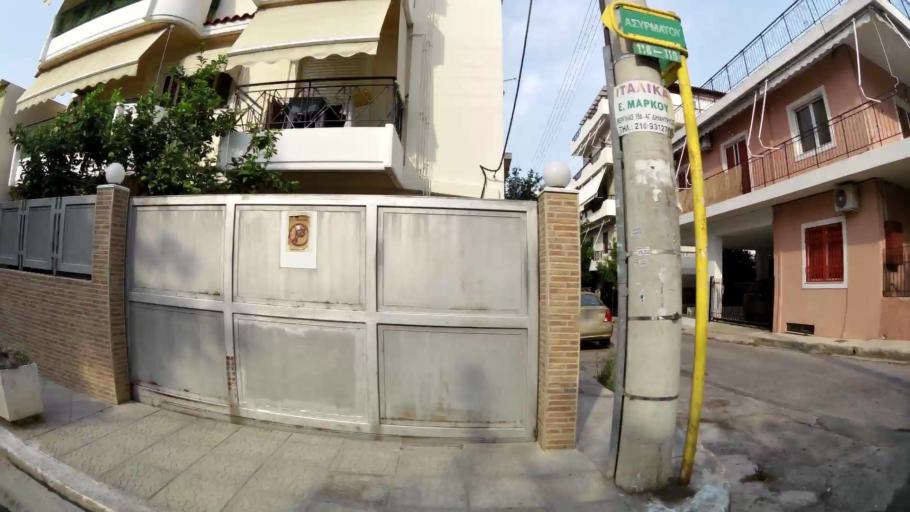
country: GR
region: Attica
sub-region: Nomarchia Athinas
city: Agios Dimitrios
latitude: 37.9301
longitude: 23.7203
